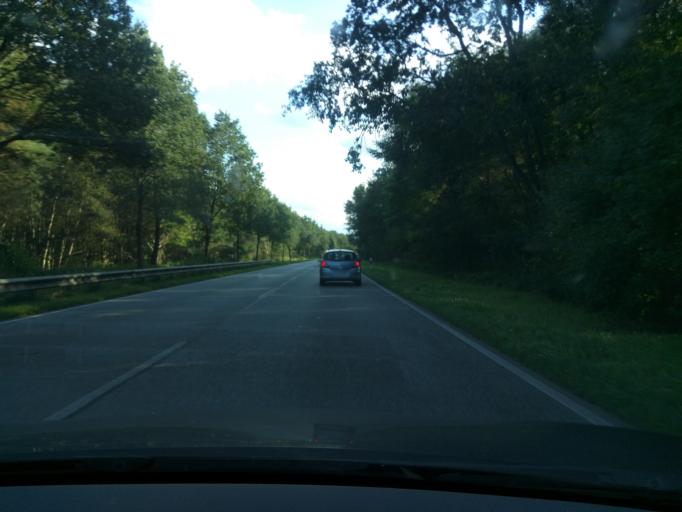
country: DE
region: Schleswig-Holstein
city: Escheburg
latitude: 53.4458
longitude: 10.3366
